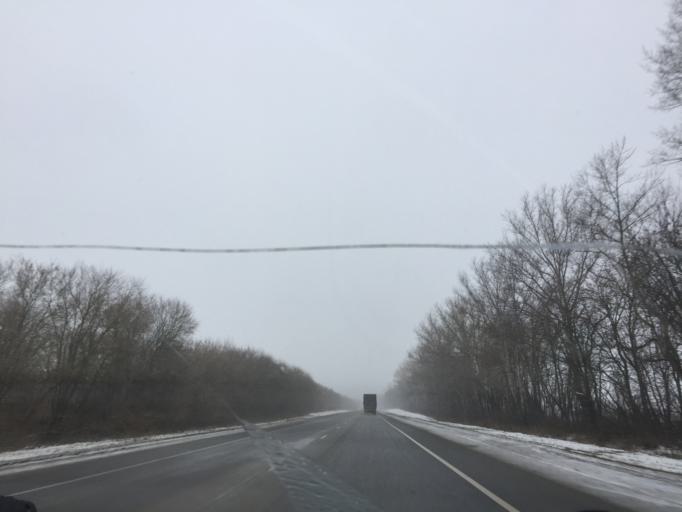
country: RU
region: Tula
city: Plavsk
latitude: 53.7714
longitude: 37.3492
